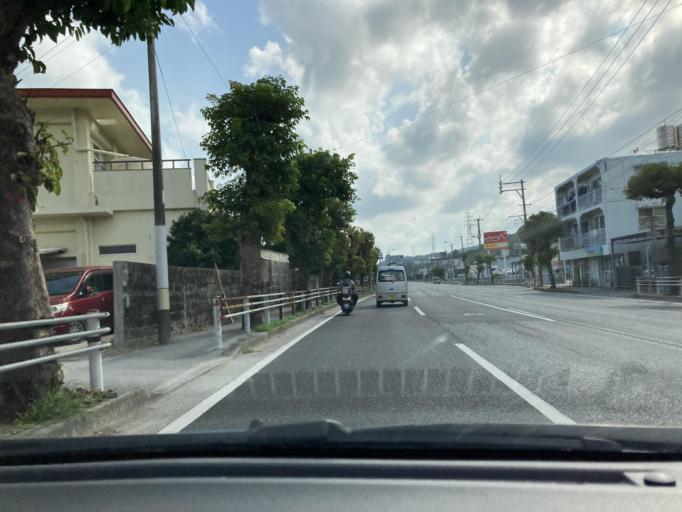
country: JP
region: Okinawa
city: Ginowan
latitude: 26.2640
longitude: 127.7895
